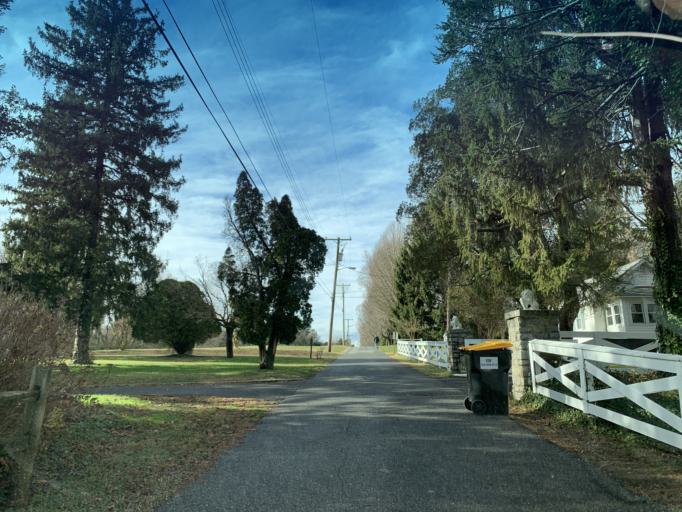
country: US
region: Maryland
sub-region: Harford County
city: Aberdeen Proving Ground
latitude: 39.3696
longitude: -76.0540
